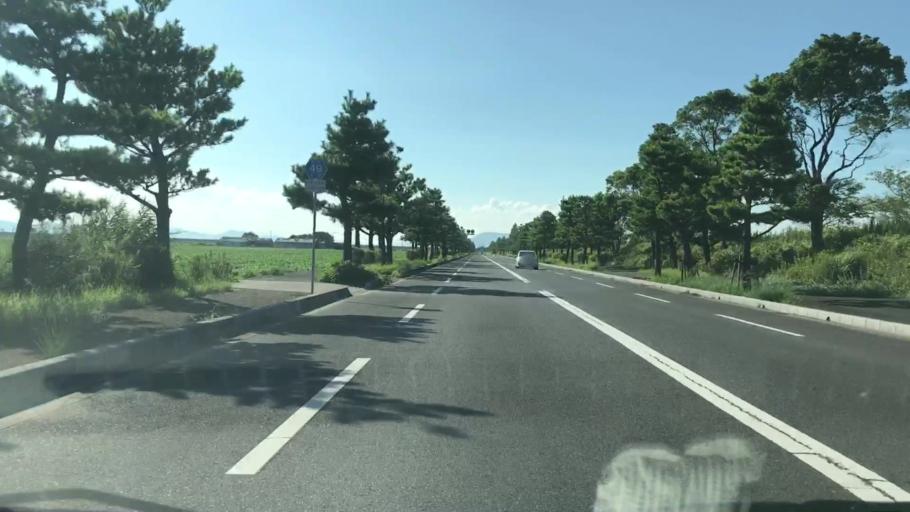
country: JP
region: Saga Prefecture
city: Okawa
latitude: 33.1557
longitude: 130.3008
